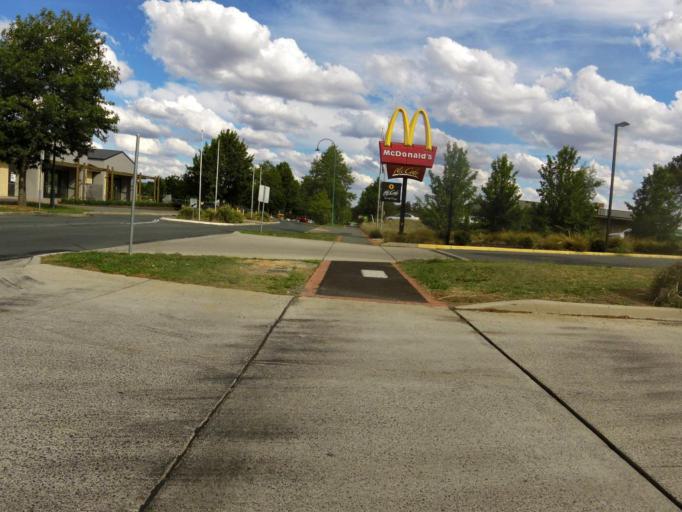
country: AU
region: Australian Capital Territory
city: Belconnen
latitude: -35.1893
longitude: 149.0821
